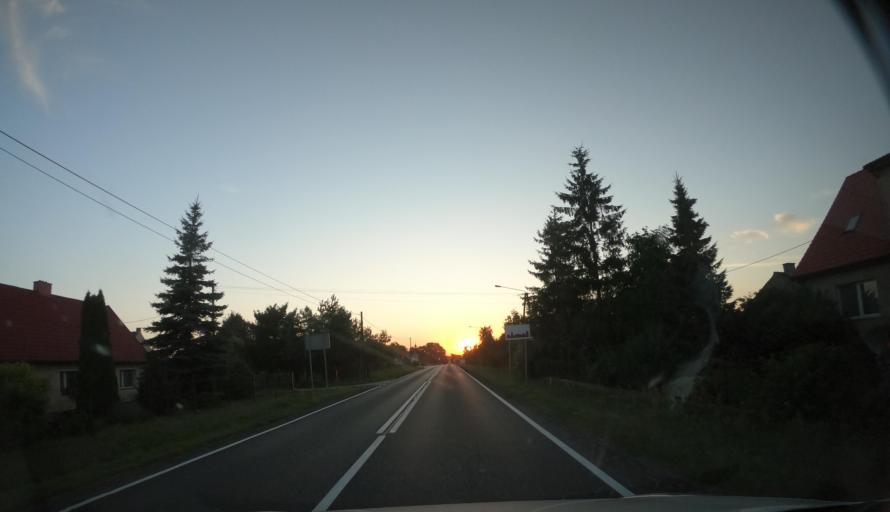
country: PL
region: Kujawsko-Pomorskie
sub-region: Powiat bydgoski
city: Koronowo
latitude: 53.3432
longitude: 17.8677
